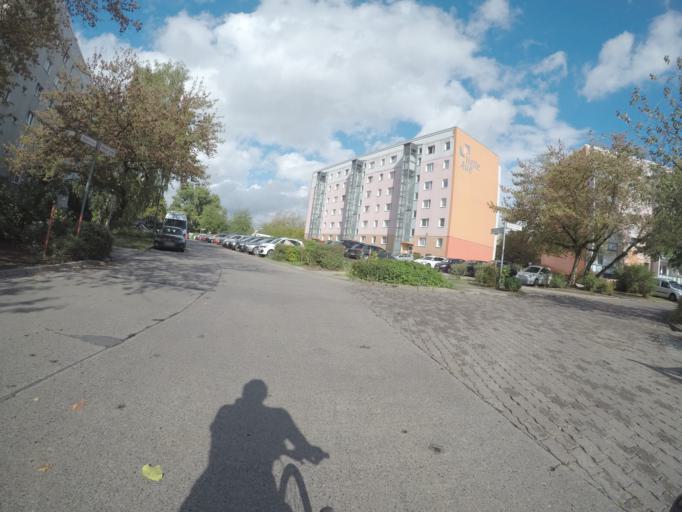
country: DE
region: Berlin
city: Falkenberg
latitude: 52.5670
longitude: 13.5562
